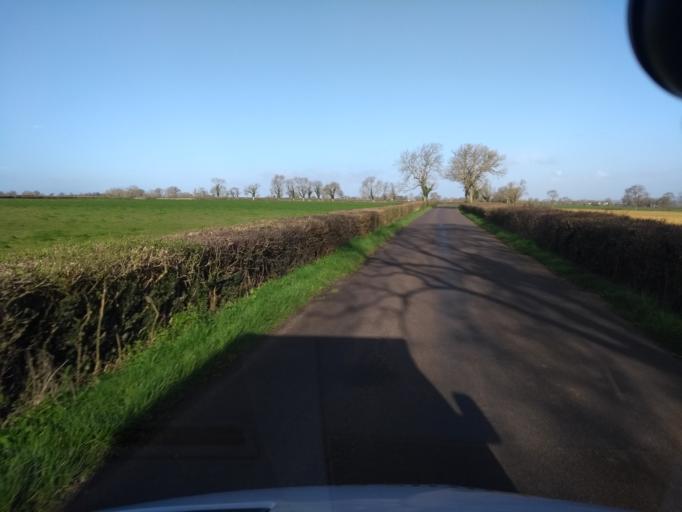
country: GB
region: England
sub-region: Somerset
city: Westonzoyland
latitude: 51.1382
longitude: -2.8485
